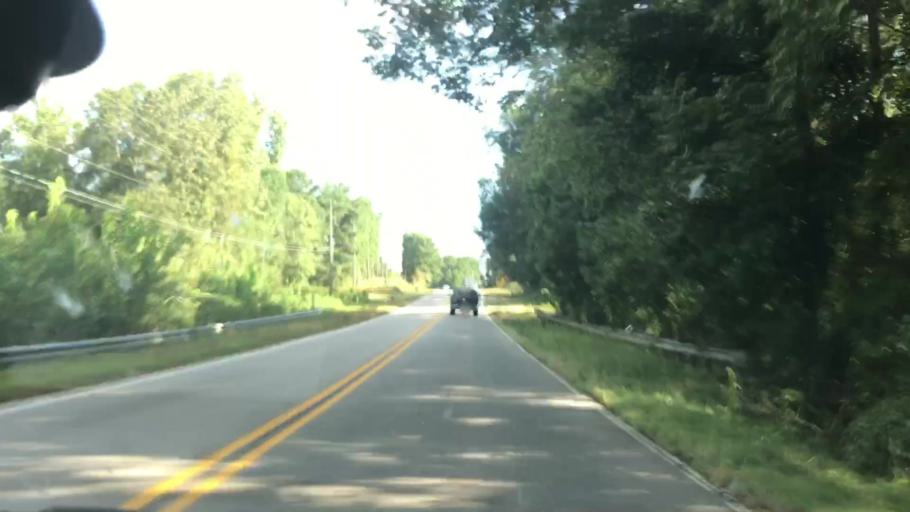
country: US
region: Georgia
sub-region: Troup County
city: La Grange
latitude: 32.9684
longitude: -84.9854
